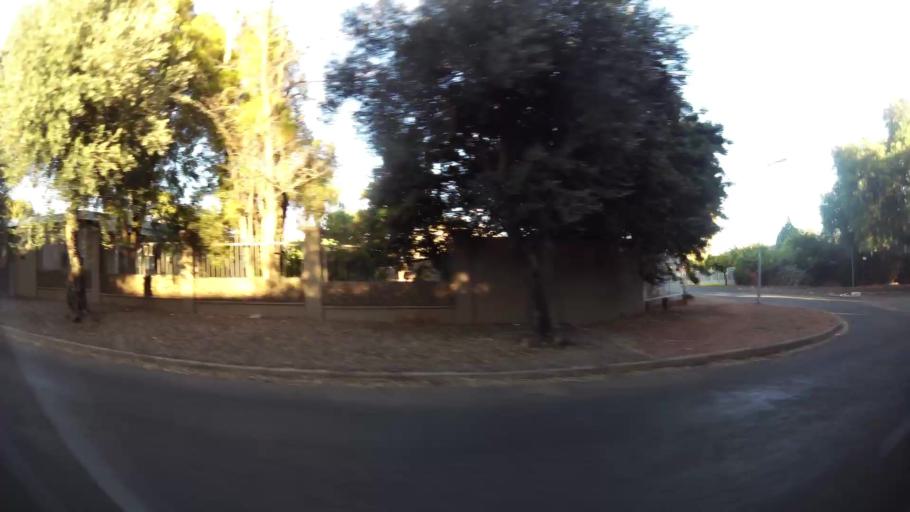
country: ZA
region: Northern Cape
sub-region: Frances Baard District Municipality
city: Kimberley
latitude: -28.7539
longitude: 24.7368
